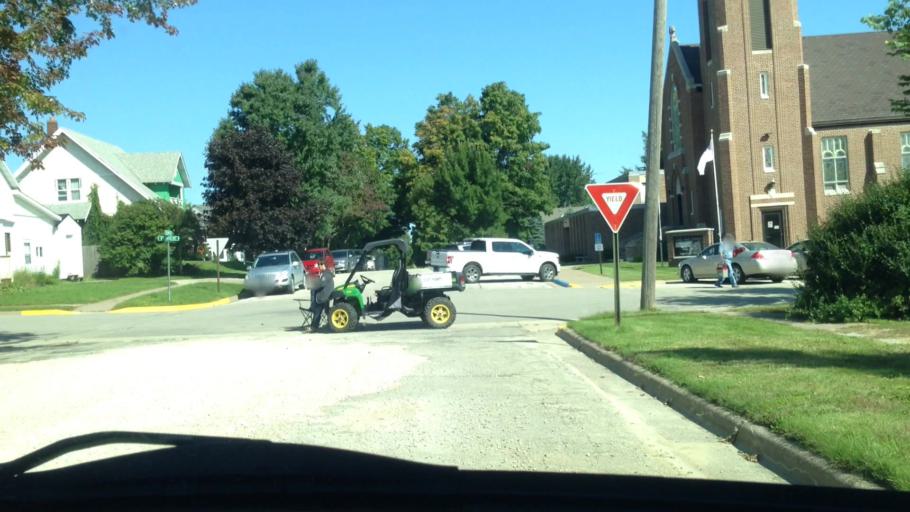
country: US
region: Minnesota
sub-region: Houston County
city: Spring Grove
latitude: 43.5213
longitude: -91.7723
